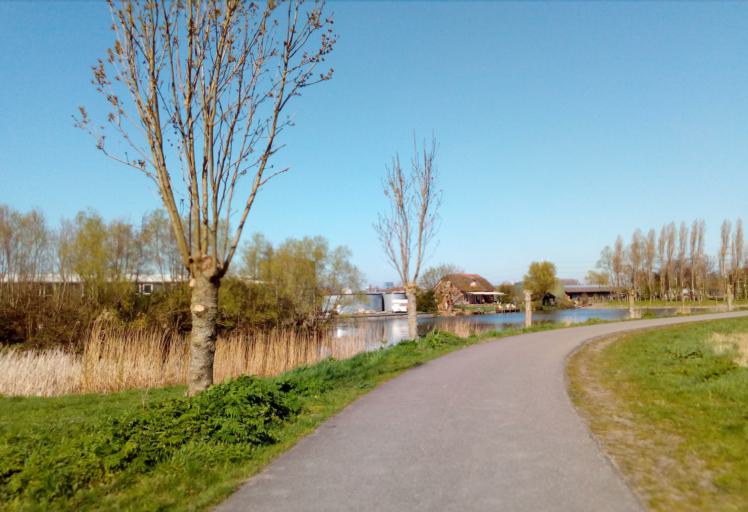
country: NL
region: South Holland
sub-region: Gemeente Rijswijk
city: Rijswijk
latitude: 52.0044
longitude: 4.3008
